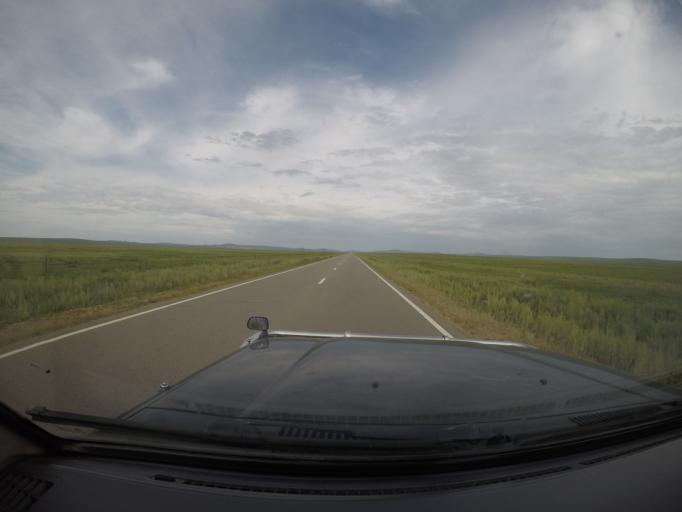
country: MN
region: Suhbaatar
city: Hanhohiy
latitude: 47.5671
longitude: 112.2676
